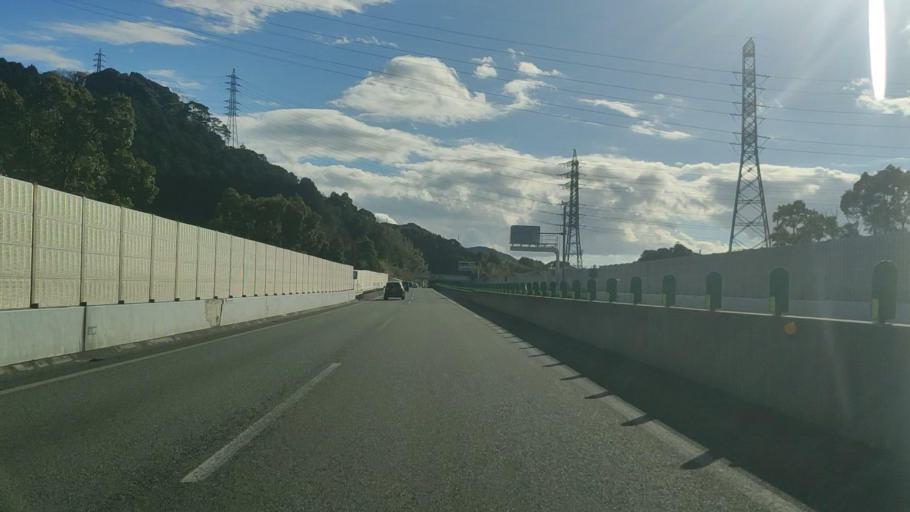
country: JP
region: Fukuoka
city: Kitakyushu
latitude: 33.8369
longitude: 130.7655
